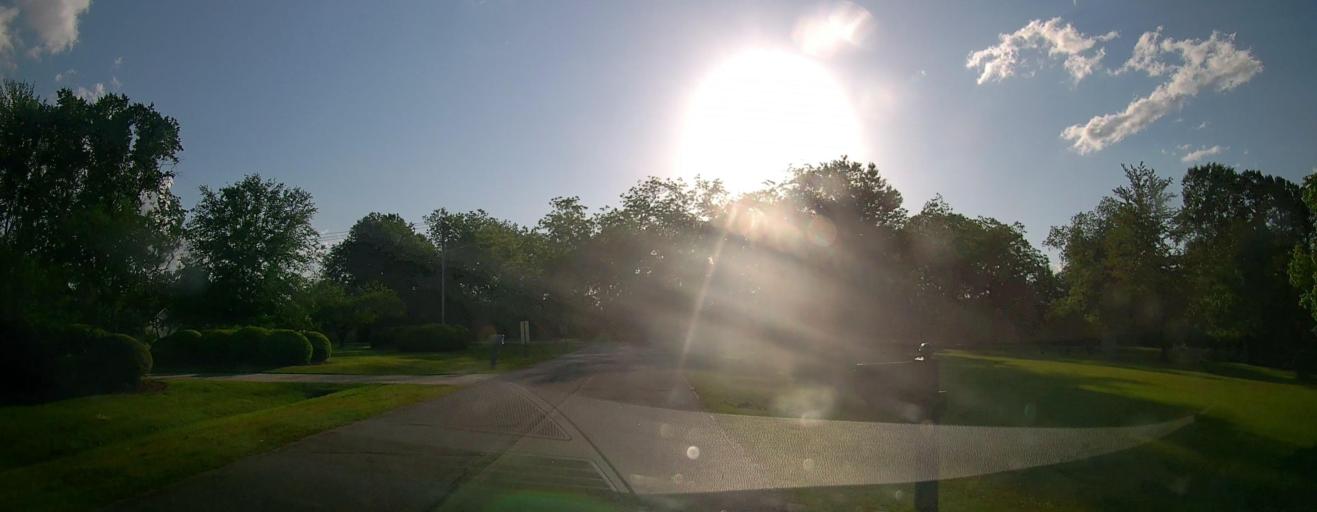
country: US
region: Georgia
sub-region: Peach County
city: Byron
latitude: 32.6383
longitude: -83.7564
